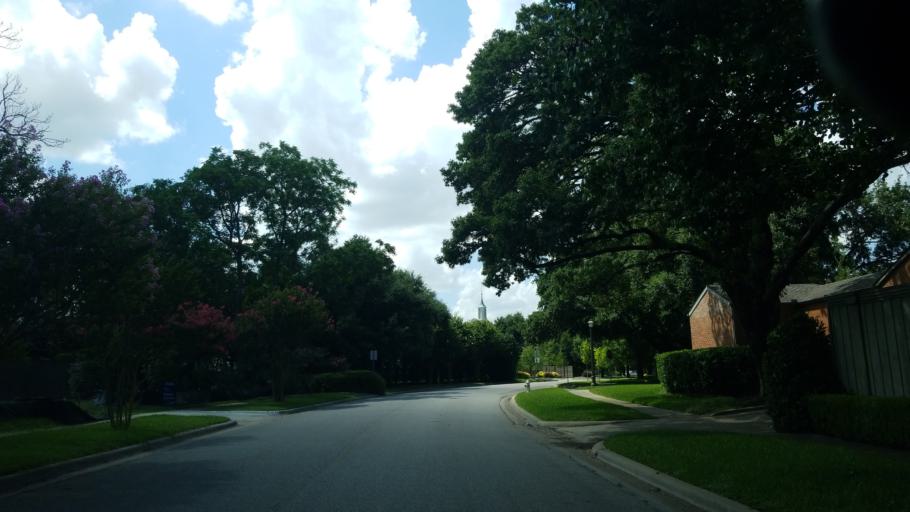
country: US
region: Texas
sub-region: Dallas County
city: Highland Park
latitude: 32.8283
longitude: -96.8185
